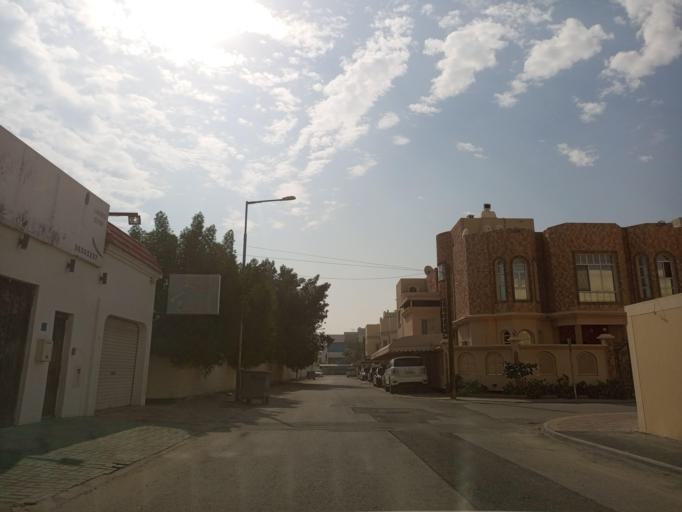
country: BH
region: Muharraq
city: Al Hadd
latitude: 26.2547
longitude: 50.6421
